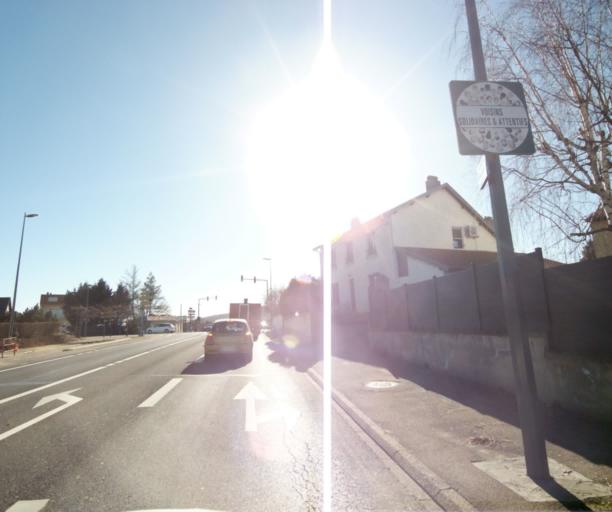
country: FR
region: Lorraine
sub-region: Departement de Meurthe-et-Moselle
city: Vandoeuvre-les-Nancy
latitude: 48.6532
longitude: 6.1852
